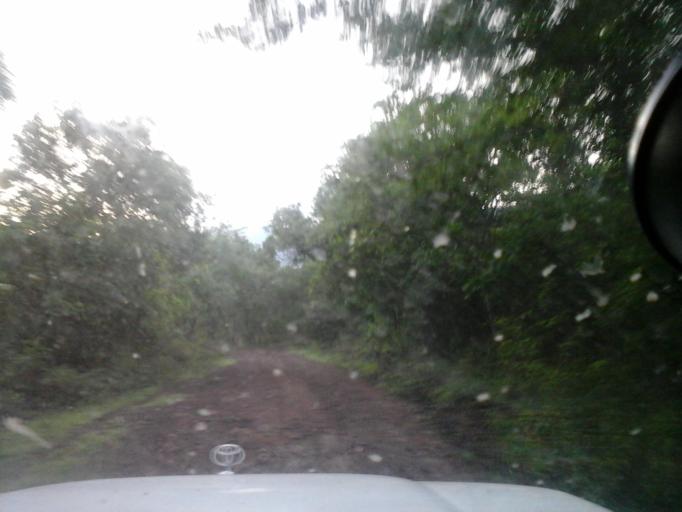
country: CO
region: Cesar
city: Agustin Codazzi
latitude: 10.1708
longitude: -73.1704
